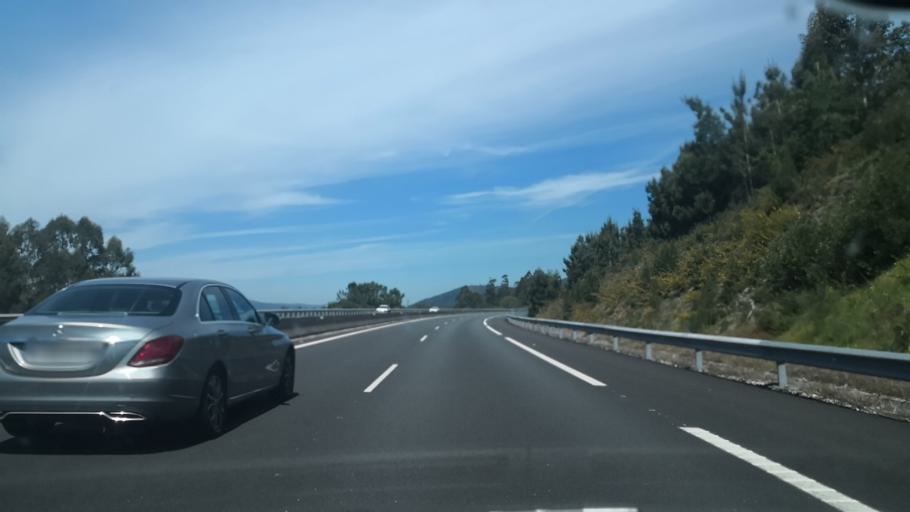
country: ES
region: Galicia
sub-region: Provincia de Pontevedra
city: Valga
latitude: 42.7141
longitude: -8.6436
